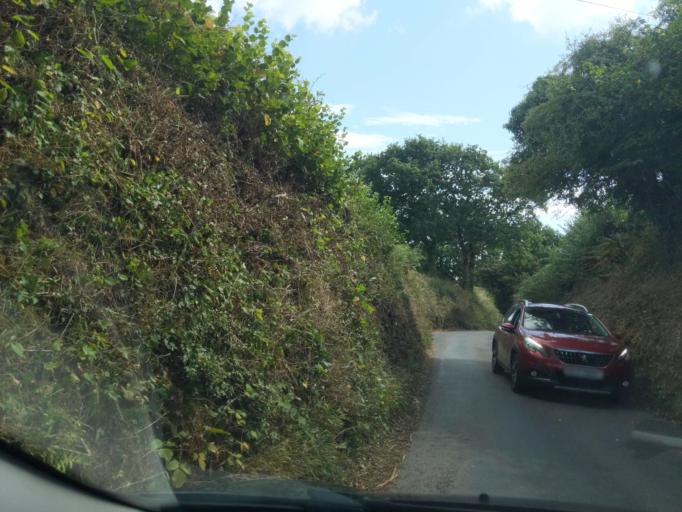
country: GB
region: England
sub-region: Devon
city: Modbury
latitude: 50.3604
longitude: -3.8955
